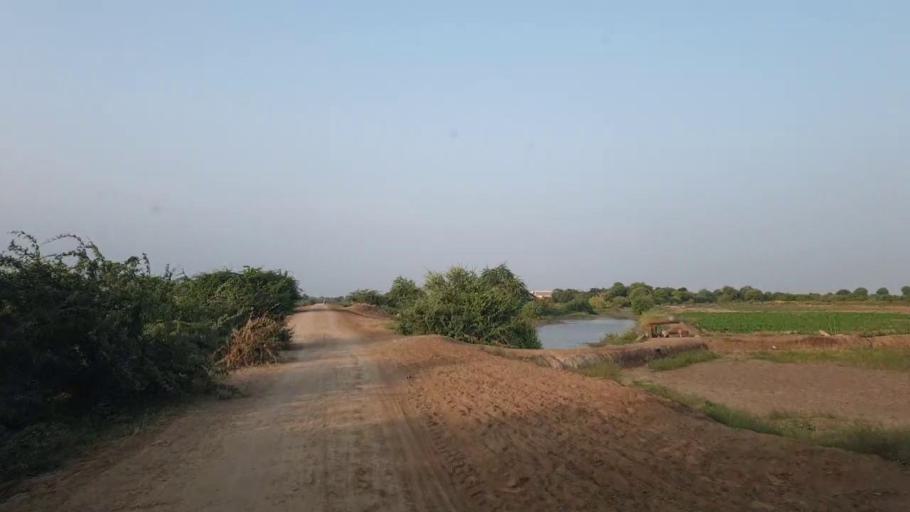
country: PK
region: Sindh
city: Tando Ghulam Ali
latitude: 25.0478
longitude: 68.9644
